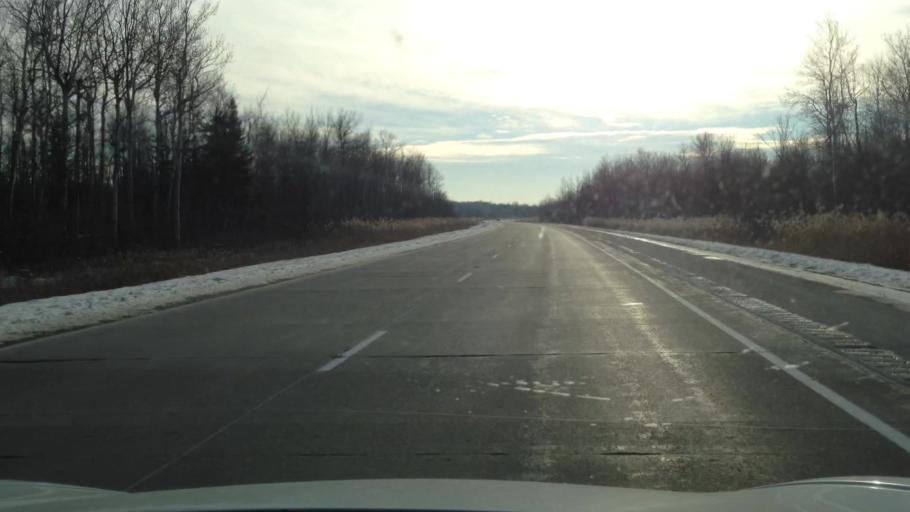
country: CA
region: Ontario
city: Hawkesbury
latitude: 45.4606
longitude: -74.6909
